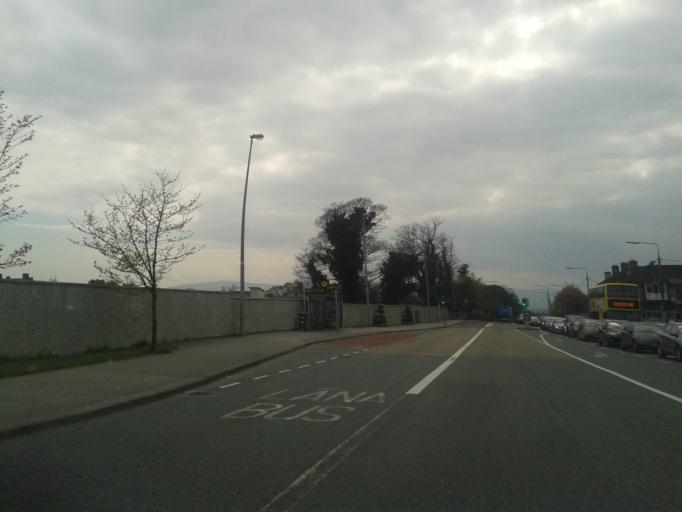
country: IE
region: Leinster
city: Beaumont
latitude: 53.3819
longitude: -6.2446
